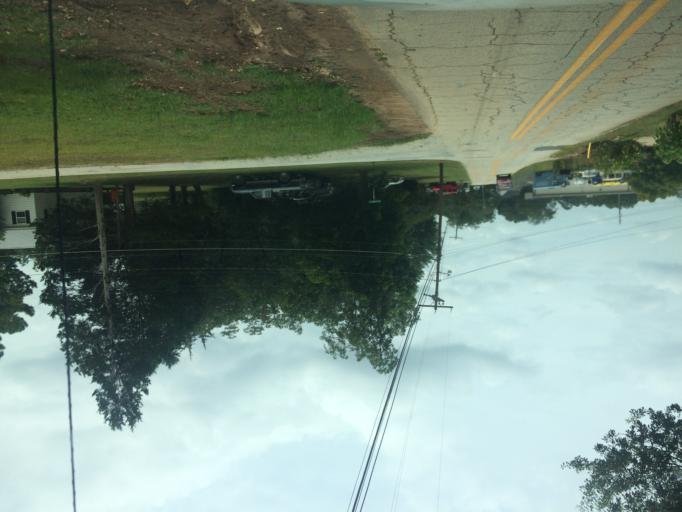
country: US
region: Georgia
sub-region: Elbert County
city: Elberton
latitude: 34.1287
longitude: -82.8613
